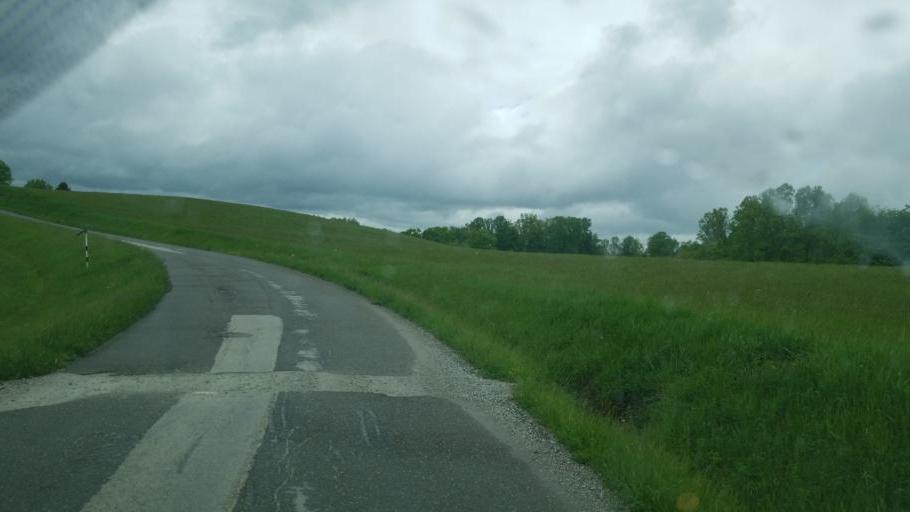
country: US
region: Ohio
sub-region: Tuscarawas County
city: Rockford
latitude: 40.3984
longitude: -81.1893
